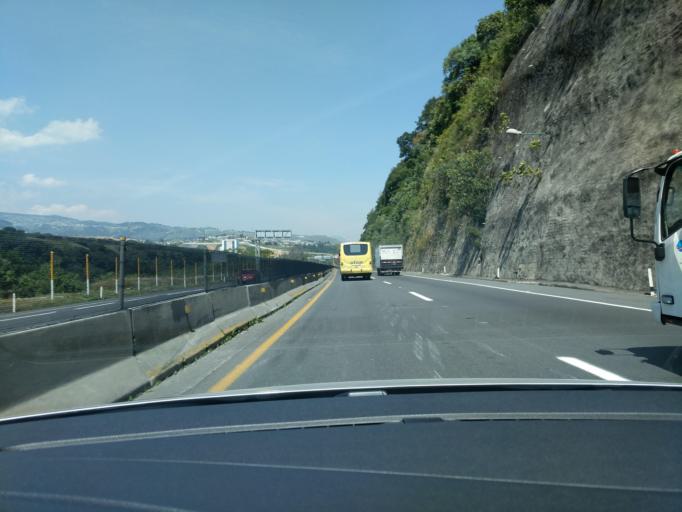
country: MX
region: Mexico
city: San Bartolome Coatepec
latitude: 19.3970
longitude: -99.2964
